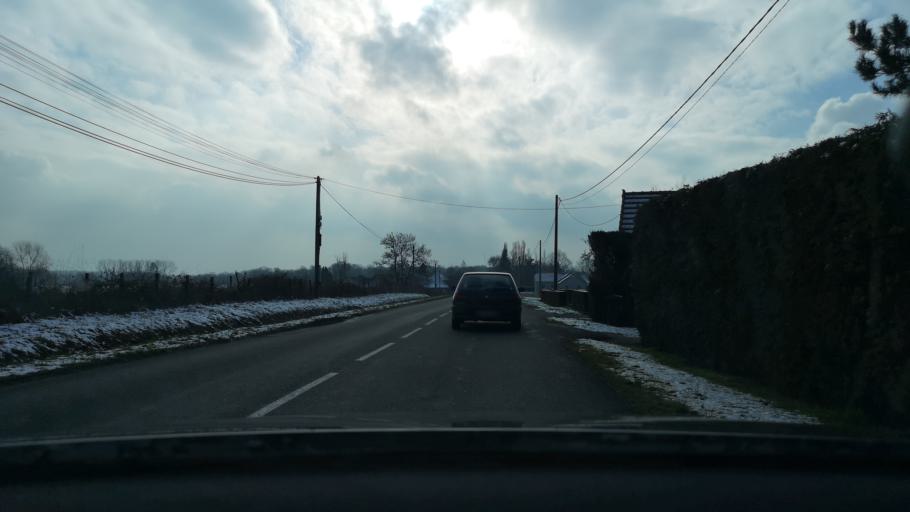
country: FR
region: Bourgogne
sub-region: Departement de Saone-et-Loire
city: Saint-Usuge
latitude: 46.6989
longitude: 5.3564
